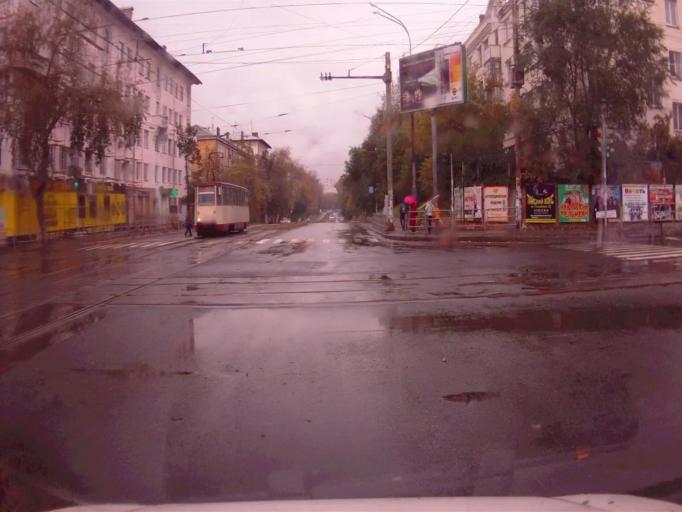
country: RU
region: Chelyabinsk
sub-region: Gorod Chelyabinsk
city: Chelyabinsk
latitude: 55.1854
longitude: 61.4142
